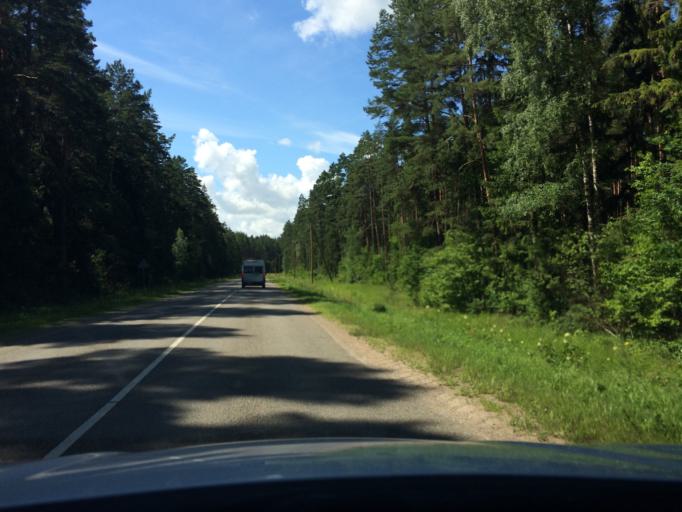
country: LV
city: Tervete
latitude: 56.4923
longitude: 23.4395
